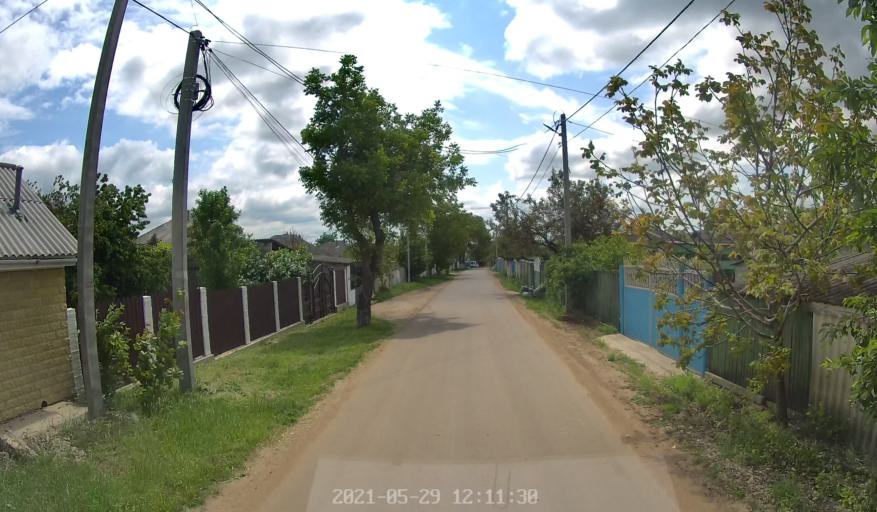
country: MD
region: Hincesti
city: Hincesti
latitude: 46.8828
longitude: 28.6298
